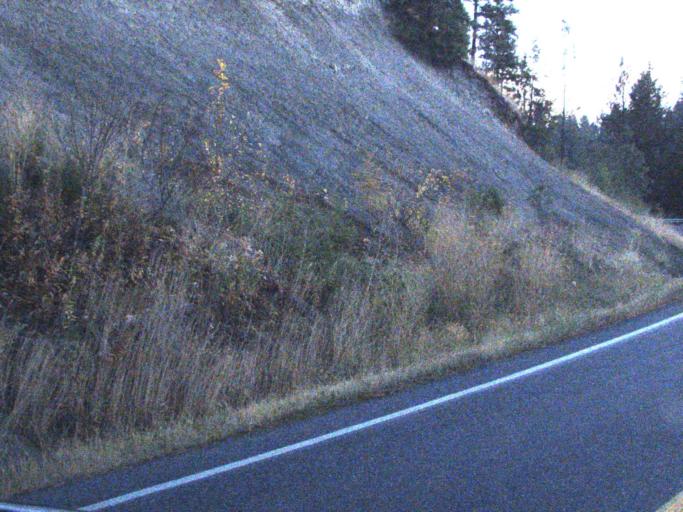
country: US
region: Washington
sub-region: Stevens County
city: Kettle Falls
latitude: 48.6155
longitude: -118.0778
